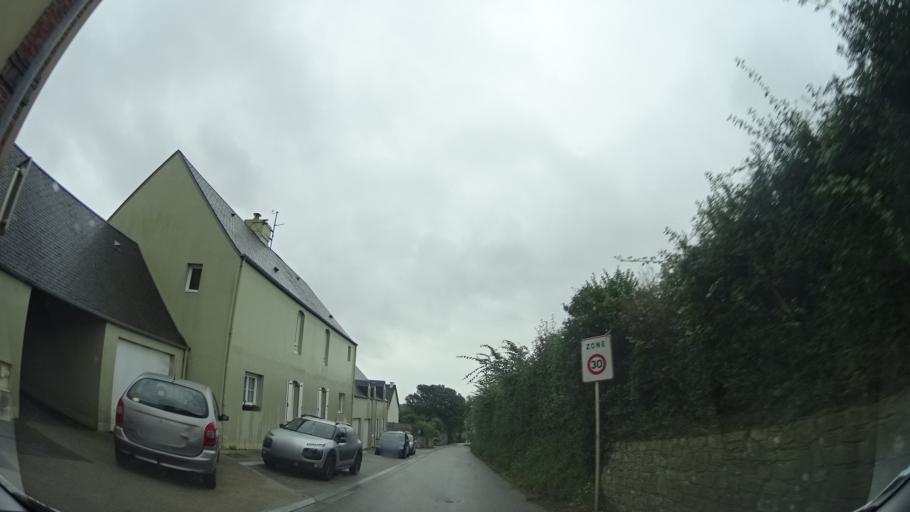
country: FR
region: Lower Normandy
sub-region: Departement de la Manche
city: Beaumont-Hague
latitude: 49.6131
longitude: -1.8237
